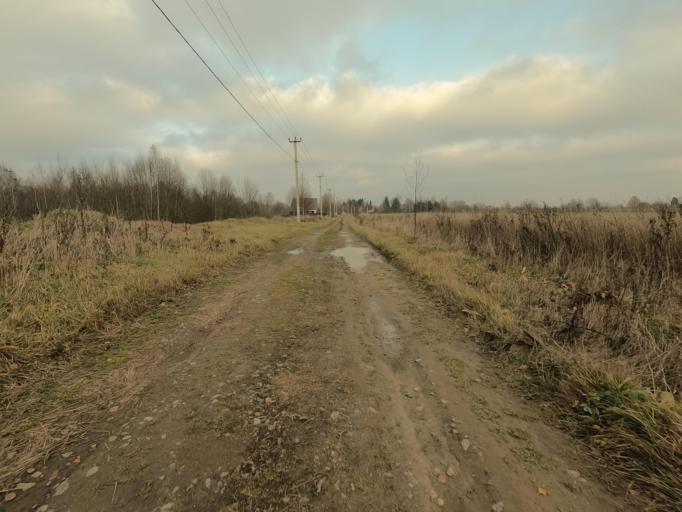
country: RU
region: Leningrad
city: Mga
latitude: 59.7548
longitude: 31.0631
